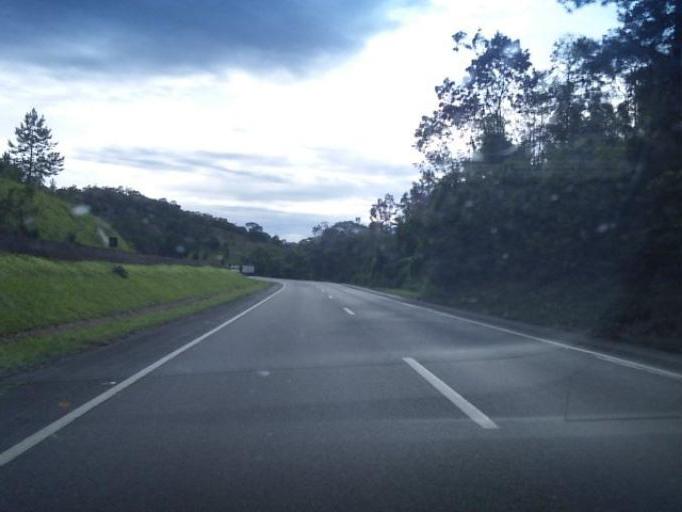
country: BR
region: Parana
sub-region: Antonina
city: Antonina
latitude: -25.1010
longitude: -48.6980
